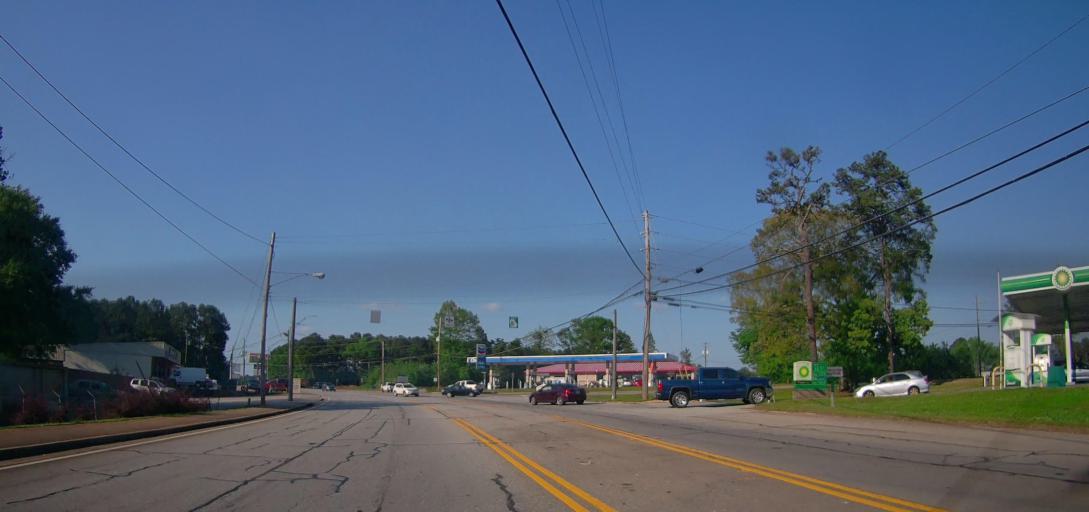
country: US
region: Georgia
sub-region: Newton County
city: Porterdale
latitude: 33.5836
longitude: -83.8779
